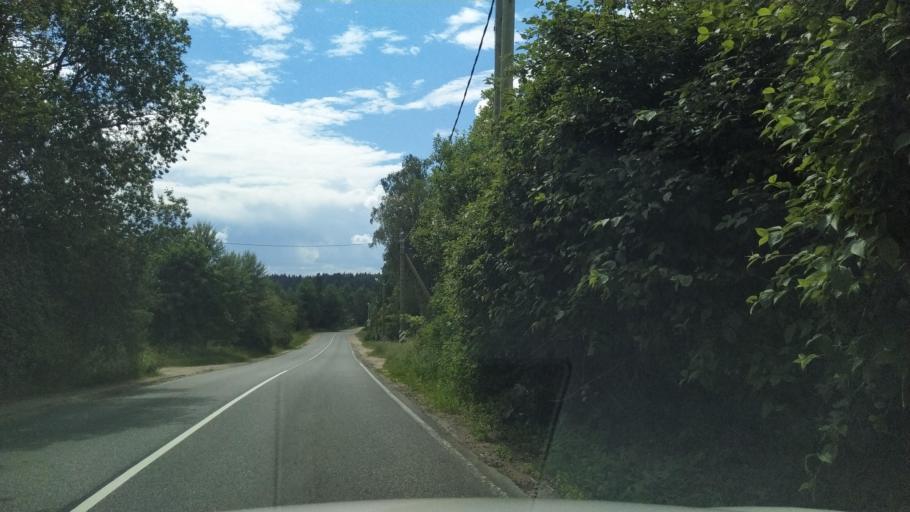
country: RU
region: Leningrad
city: Rozhdestveno
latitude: 59.3460
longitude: 29.9504
